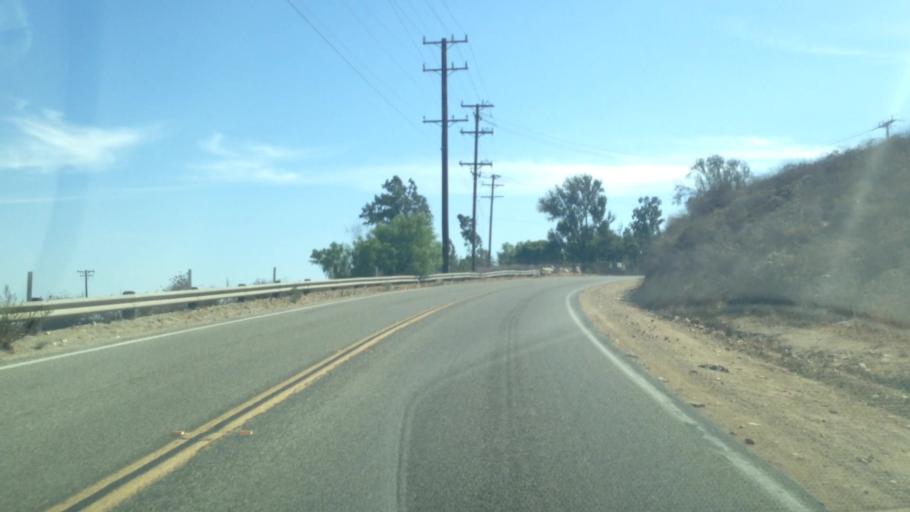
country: US
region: California
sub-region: Riverside County
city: El Cerrito
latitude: 33.8535
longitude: -117.4546
